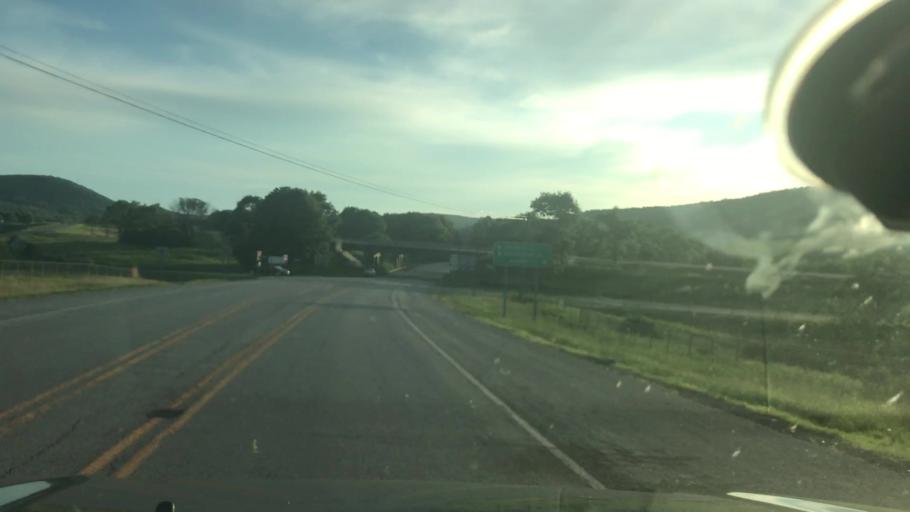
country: US
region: New York
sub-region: Otsego County
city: Unadilla
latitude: 42.3333
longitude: -75.2766
